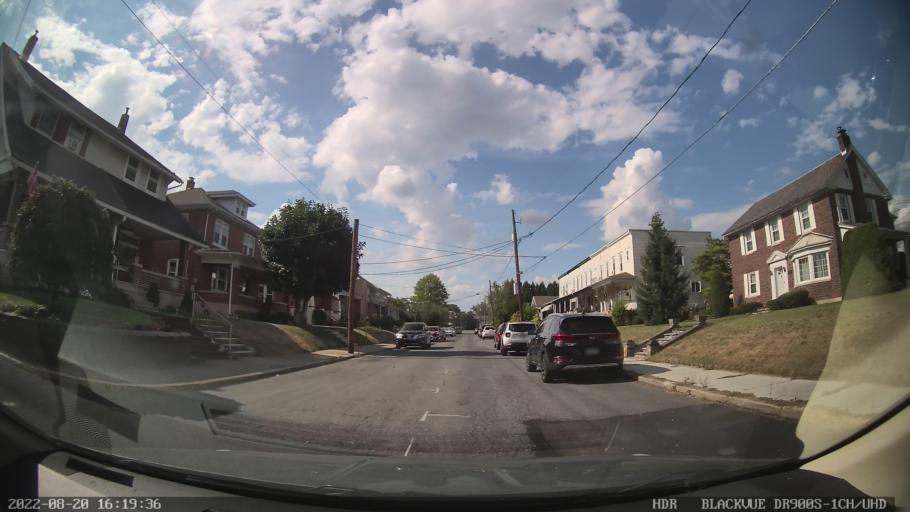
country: US
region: Pennsylvania
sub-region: Northampton County
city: Northampton
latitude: 40.6917
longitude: -75.4970
